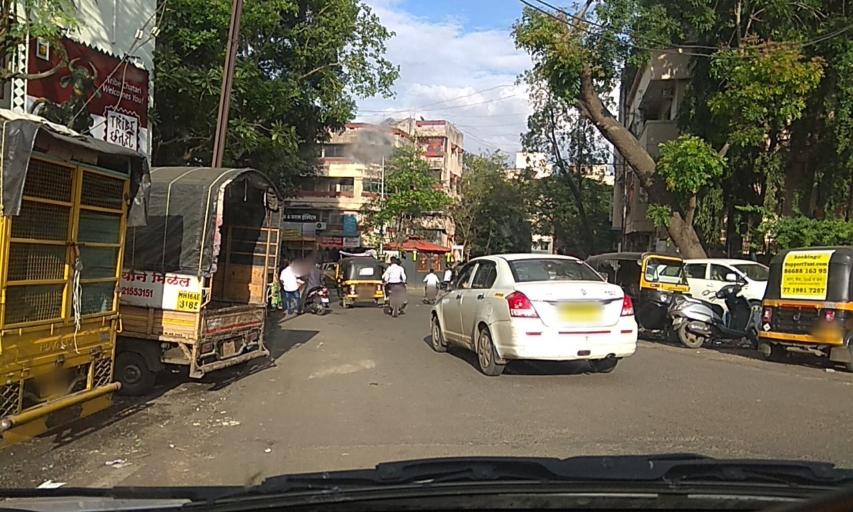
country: IN
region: Maharashtra
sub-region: Pune Division
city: Pune
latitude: 18.4982
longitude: 73.8498
